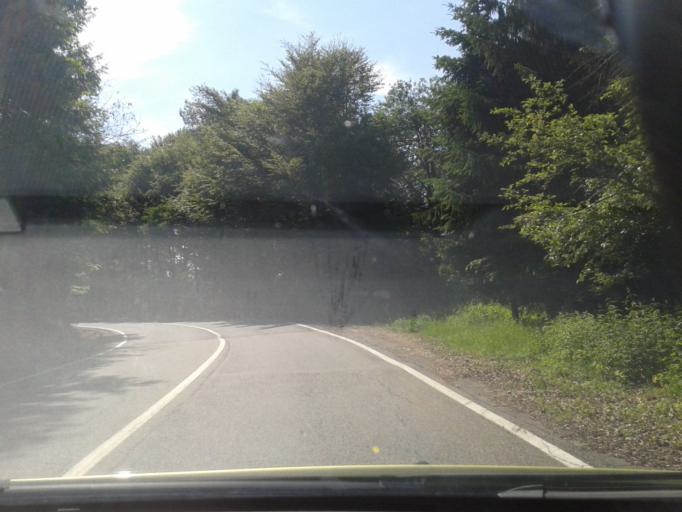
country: RO
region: Sibiu
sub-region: Comuna Cartisoara
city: Cartisoara
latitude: 45.6650
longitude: 24.5884
